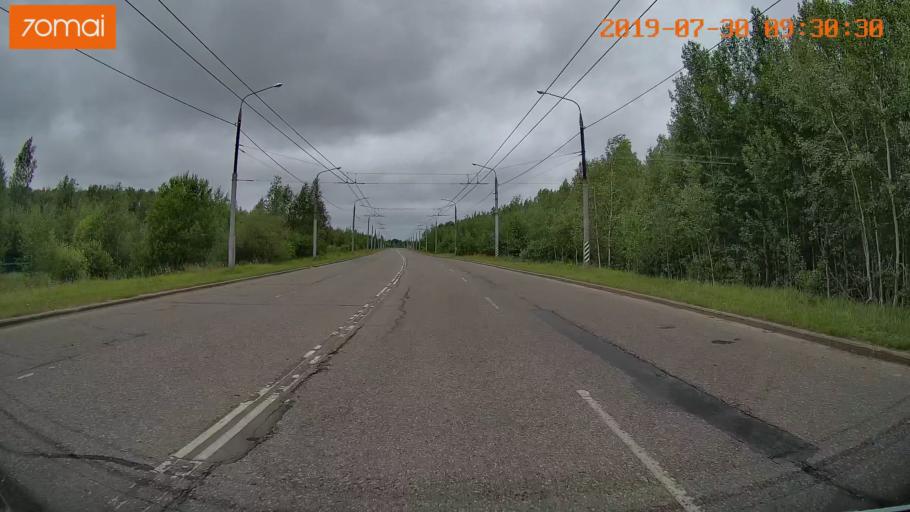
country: RU
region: Ivanovo
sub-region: Gorod Ivanovo
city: Ivanovo
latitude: 56.9452
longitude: 40.9466
